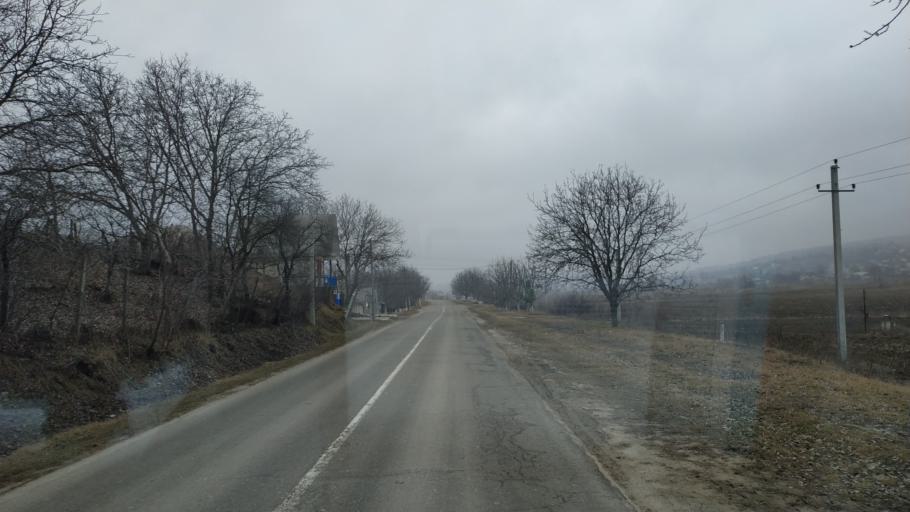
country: MD
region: Hincesti
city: Hincesti
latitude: 46.9622
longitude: 28.4845
